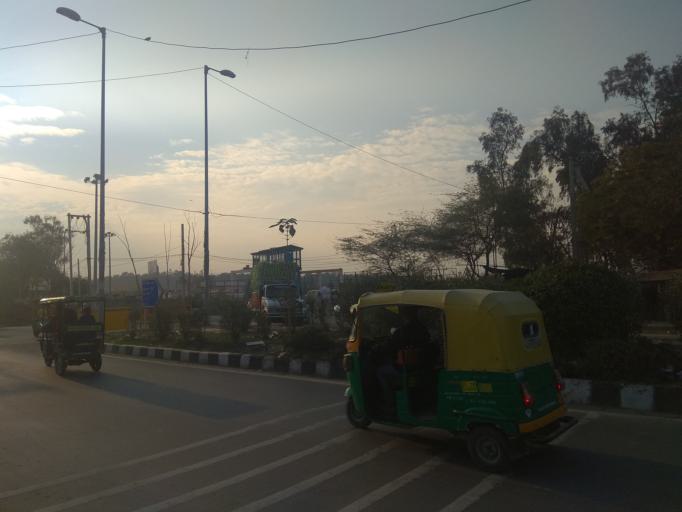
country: IN
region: NCT
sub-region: West Delhi
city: Nangloi Jat
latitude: 28.6386
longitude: 77.0610
